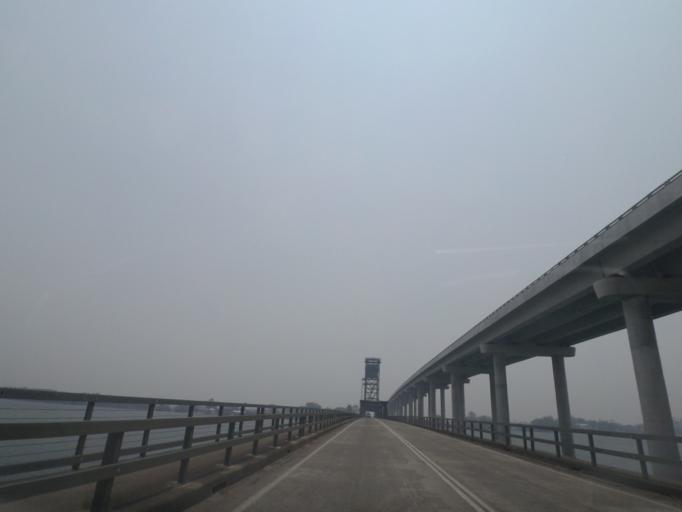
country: AU
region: New South Wales
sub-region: Clarence Valley
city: Maclean
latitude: -29.4327
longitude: 153.2407
